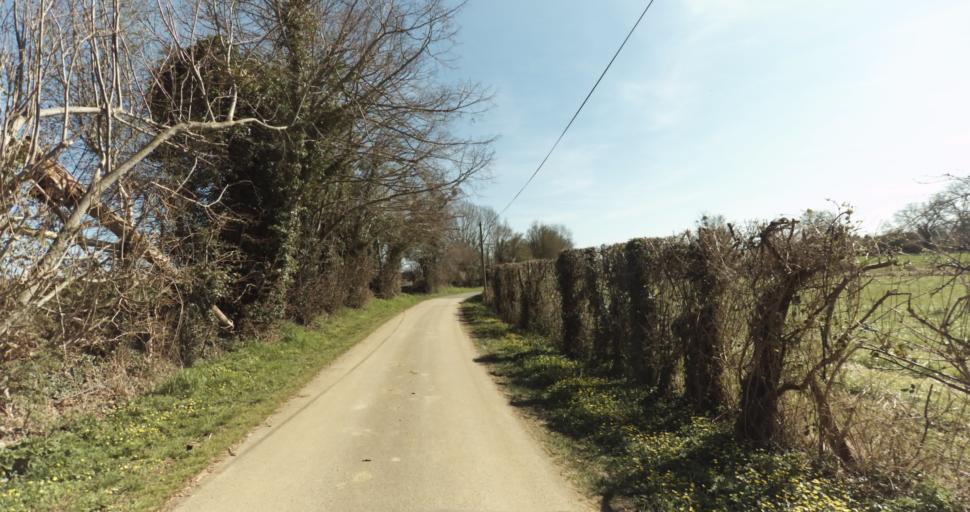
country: FR
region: Lower Normandy
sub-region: Departement du Calvados
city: Saint-Pierre-sur-Dives
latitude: 49.0667
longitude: -0.0324
